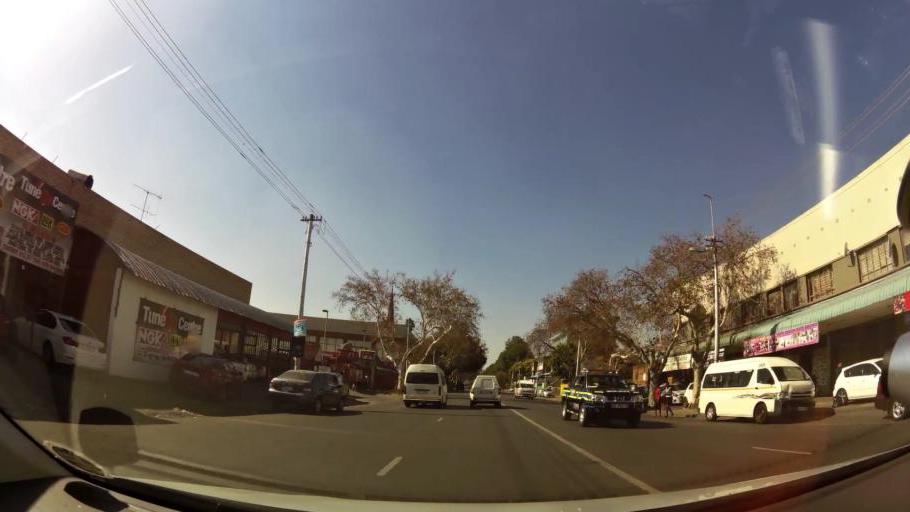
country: ZA
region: Gauteng
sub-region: City of Tshwane Metropolitan Municipality
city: Pretoria
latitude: -25.7483
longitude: 28.1608
